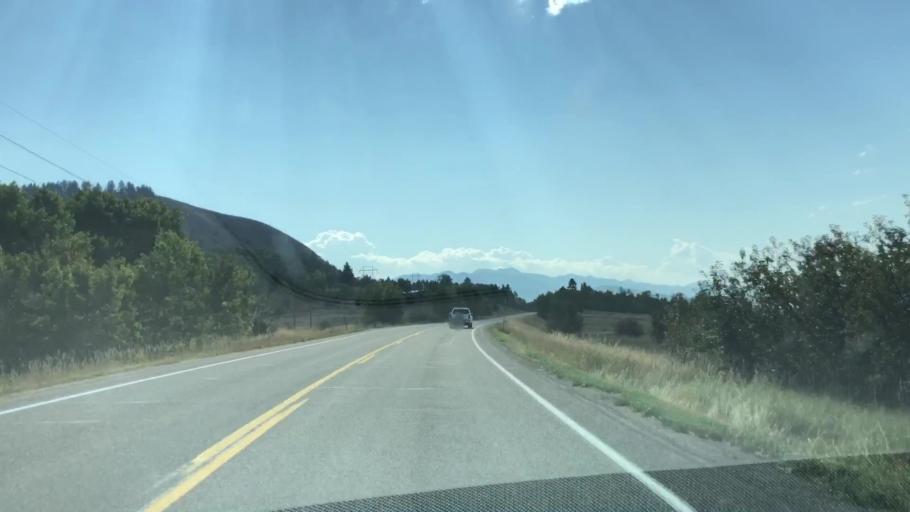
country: US
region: Wyoming
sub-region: Teton County
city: Hoback
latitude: 43.2151
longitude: -111.0630
